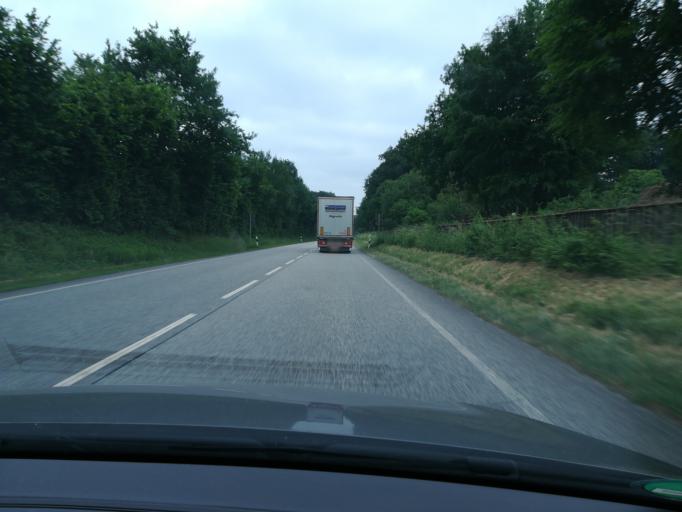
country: DE
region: Schleswig-Holstein
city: Kasseburg
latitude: 53.5518
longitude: 10.4154
